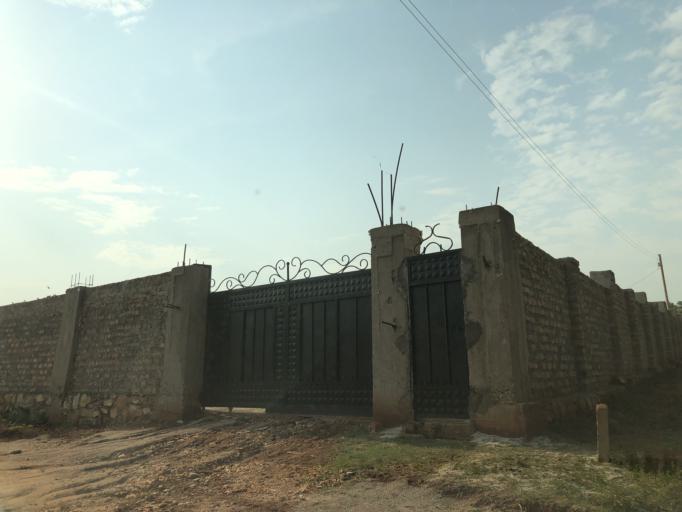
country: UG
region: Central Region
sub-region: Wakiso District
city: Bweyogerere
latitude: 0.4745
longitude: 32.6394
